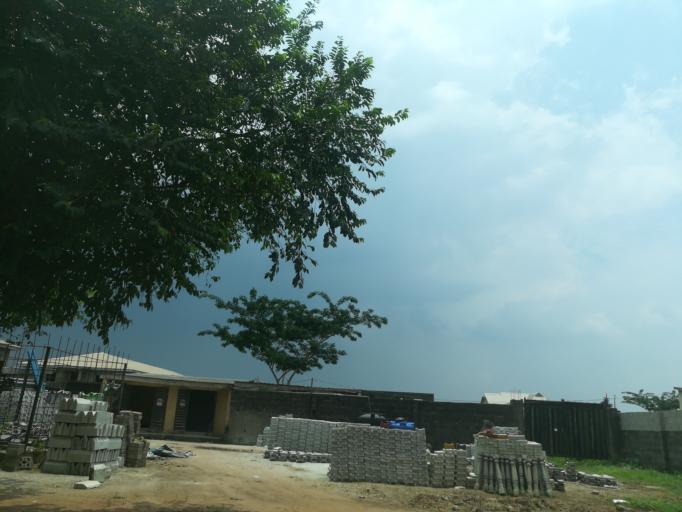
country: NG
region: Lagos
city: Ikorodu
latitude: 6.6137
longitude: 3.5739
